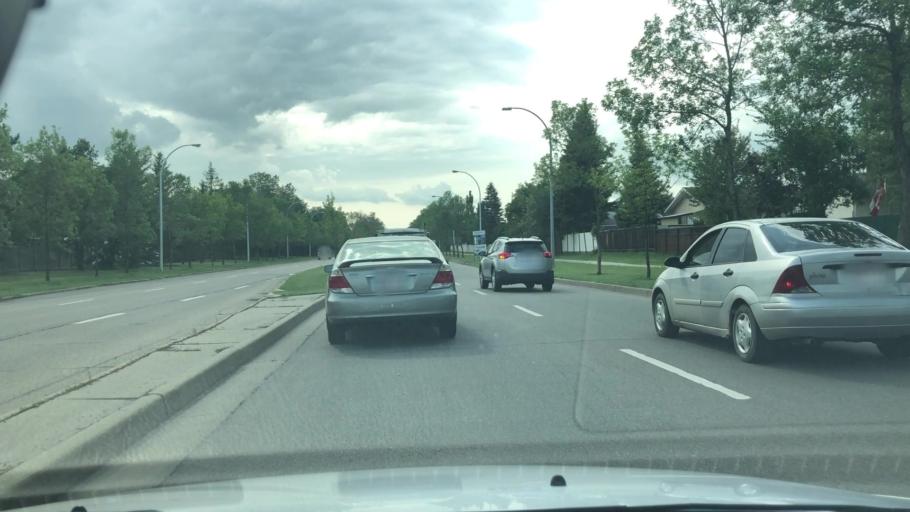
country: CA
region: Alberta
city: Edmonton
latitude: 53.6170
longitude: -113.5320
